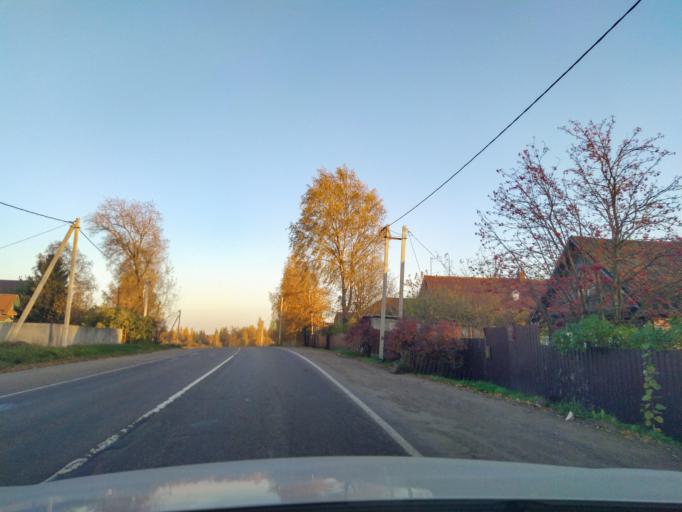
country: RU
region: Leningrad
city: Maloye Verevo
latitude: 59.6130
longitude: 30.2218
